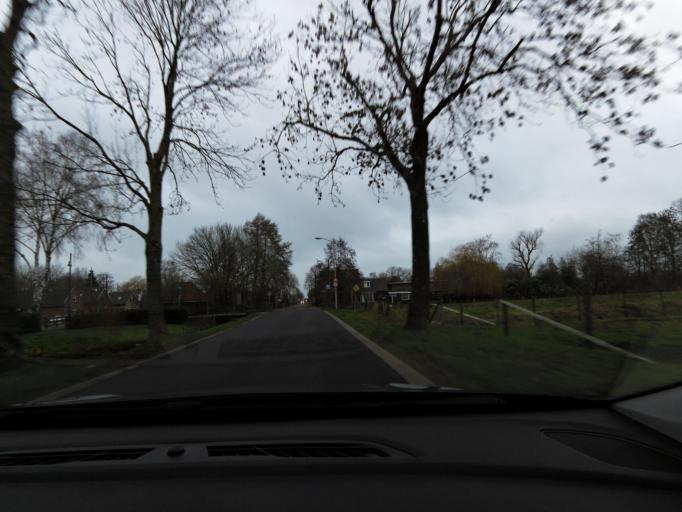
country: NL
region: North Brabant
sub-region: Gemeente Waalwijk
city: Waspik
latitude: 51.6880
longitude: 4.9842
